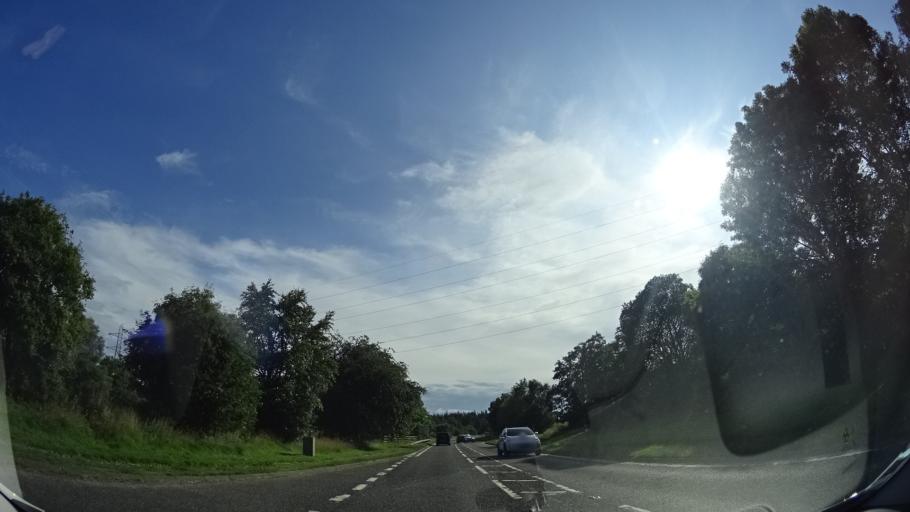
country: GB
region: Scotland
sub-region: Highland
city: Conon Bridge
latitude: 57.5758
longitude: -4.4491
